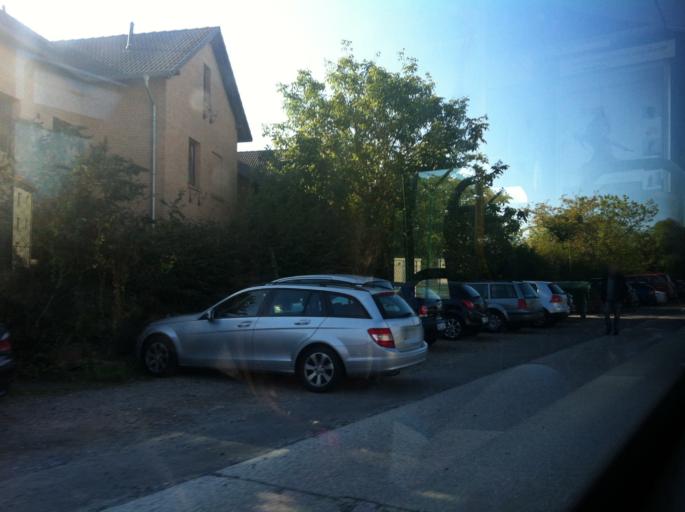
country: DE
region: Hesse
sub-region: Regierungsbezirk Darmstadt
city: Hochheim am Main
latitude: 50.0382
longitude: 8.3239
